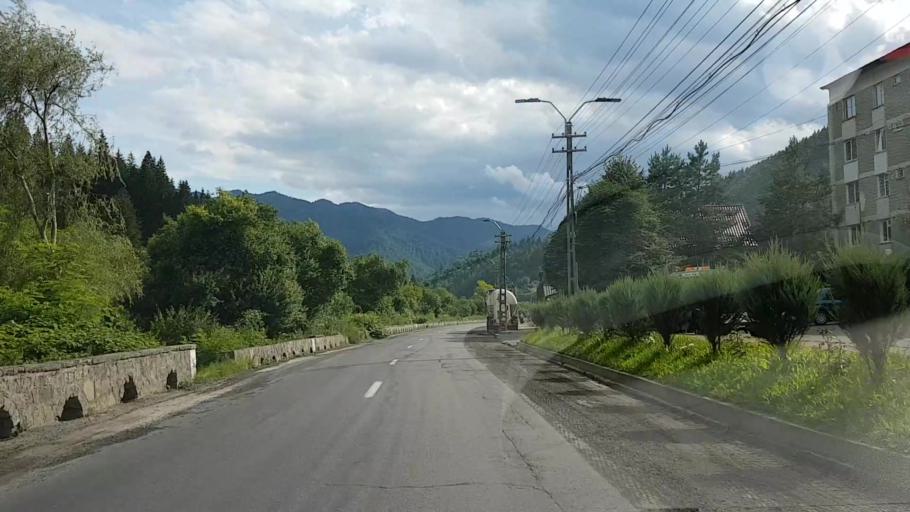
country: RO
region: Neamt
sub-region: Comuna Bicaz
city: Dodeni
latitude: 46.9252
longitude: 26.0934
